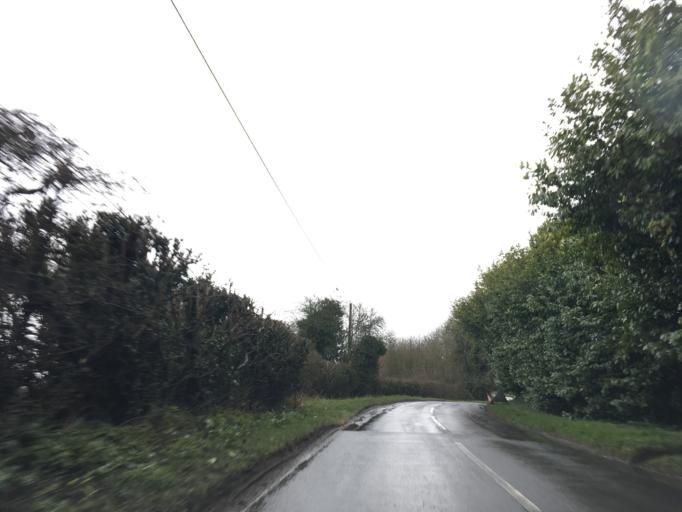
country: GB
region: England
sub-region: Borough of Swindon
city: Wanborough
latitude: 51.5440
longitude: -1.6965
